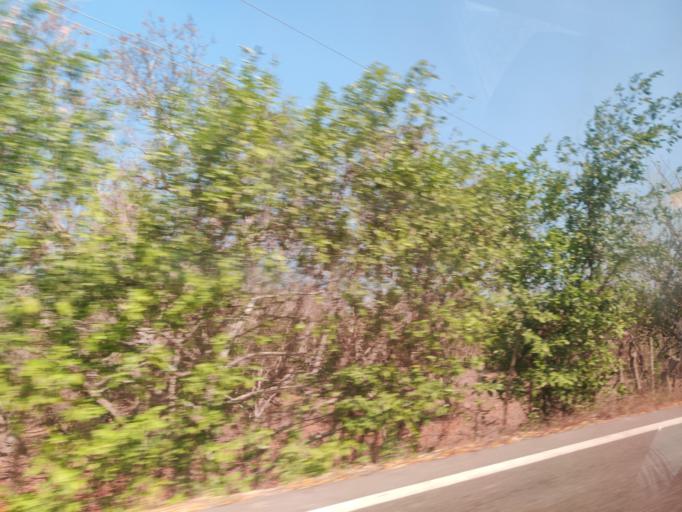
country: CO
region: Bolivar
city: Turbana
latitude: 10.1636
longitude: -75.6533
